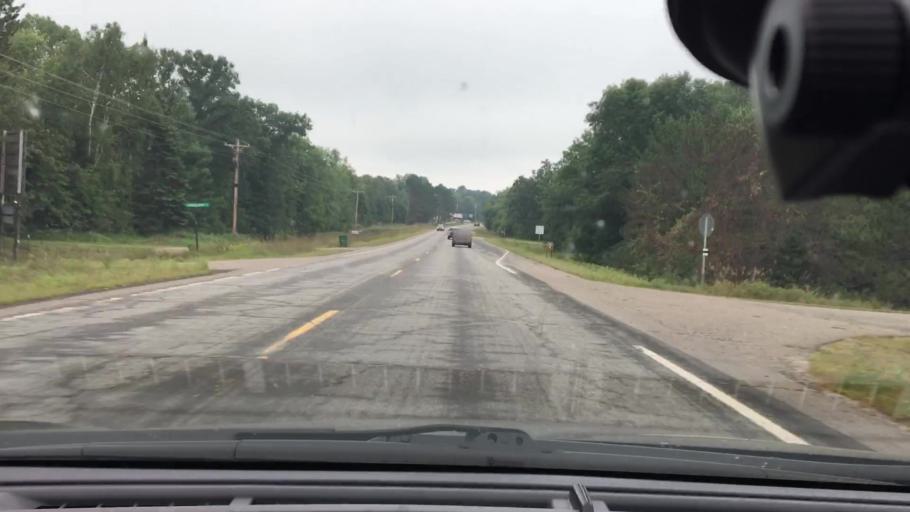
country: US
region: Minnesota
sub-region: Crow Wing County
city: Cross Lake
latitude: 46.8092
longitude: -93.9503
